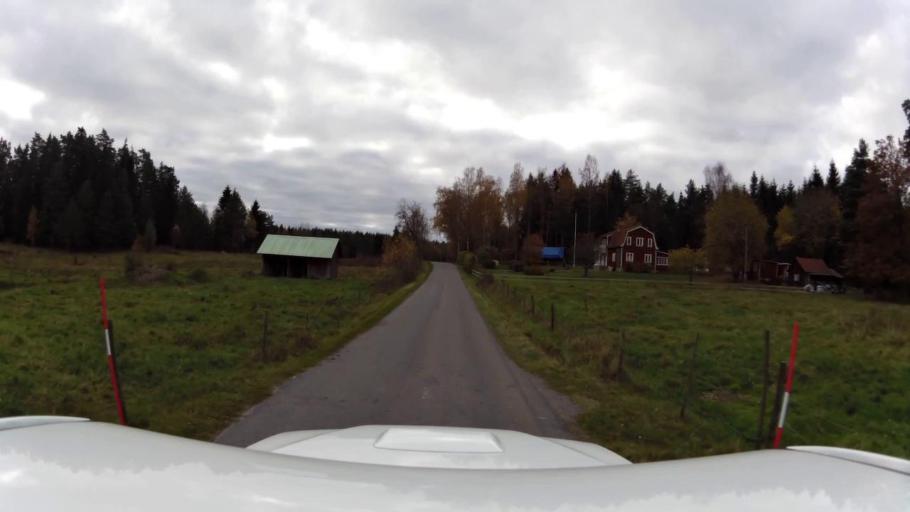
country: SE
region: OEstergoetland
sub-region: Linkopings Kommun
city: Linghem
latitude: 58.4011
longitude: 15.8442
